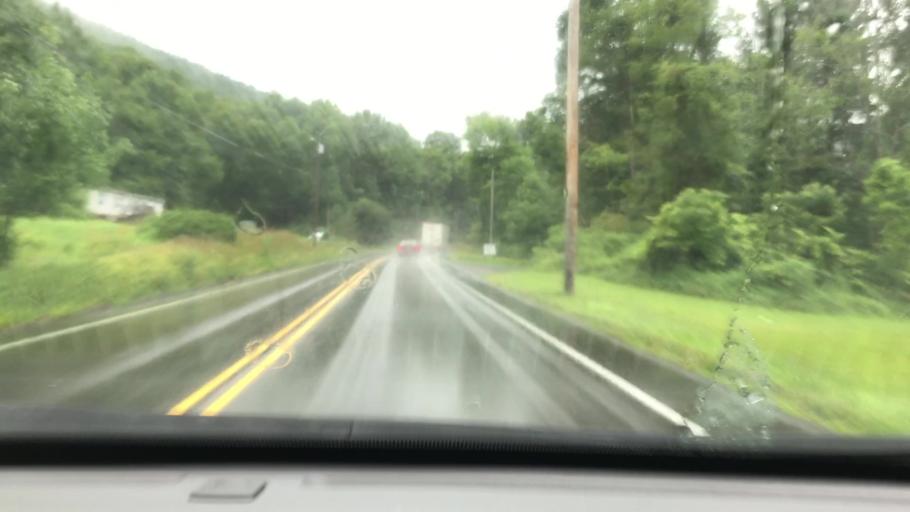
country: US
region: Pennsylvania
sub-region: Blair County
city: Tyrone
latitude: 40.7512
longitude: -78.2174
